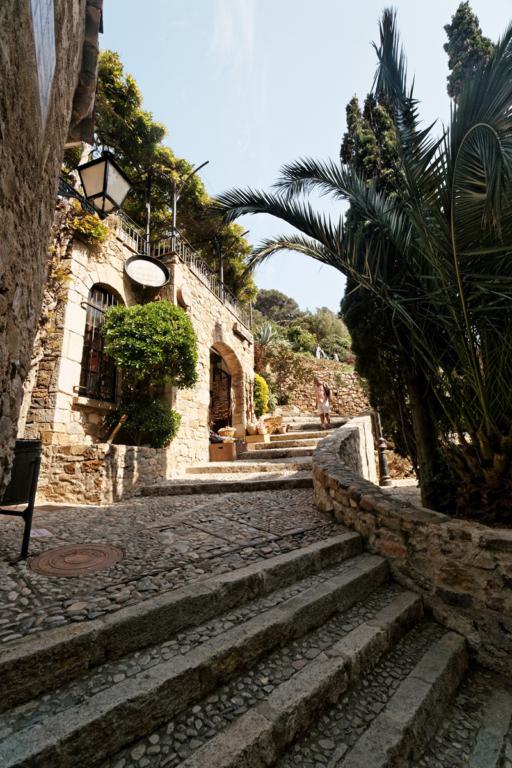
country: ES
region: Catalonia
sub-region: Provincia de Girona
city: Tossa de Mar
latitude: 41.7163
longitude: 2.9328
